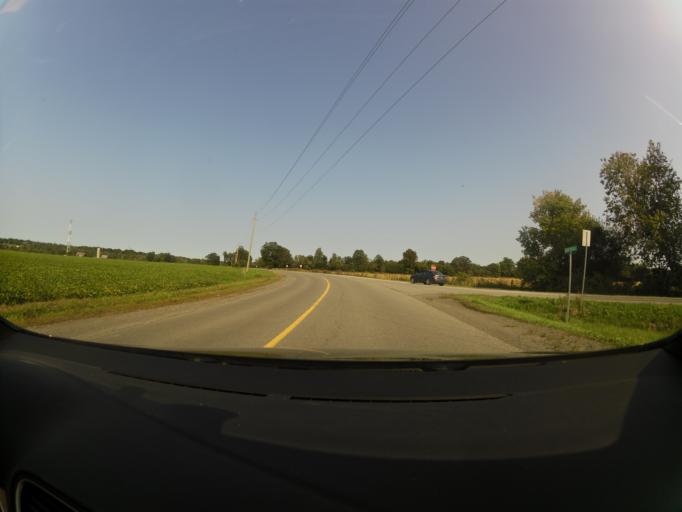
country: CA
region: Ontario
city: Bells Corners
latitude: 45.3396
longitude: -76.0510
